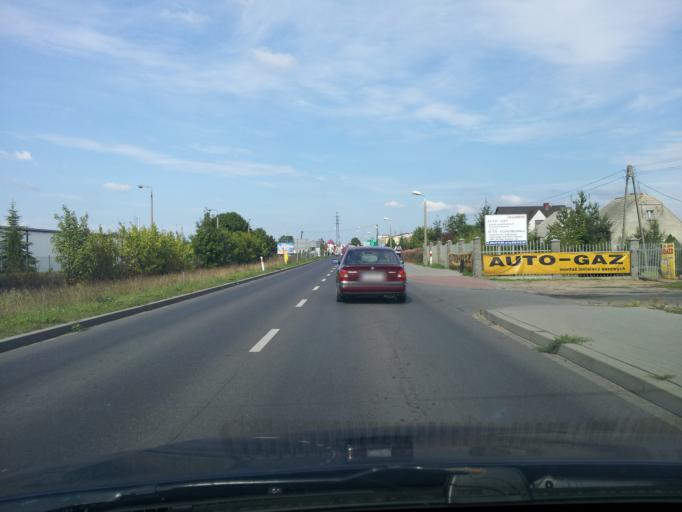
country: PL
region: Kujawsko-Pomorskie
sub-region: Powiat brodnicki
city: Brodnica
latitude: 53.2328
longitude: 19.3898
